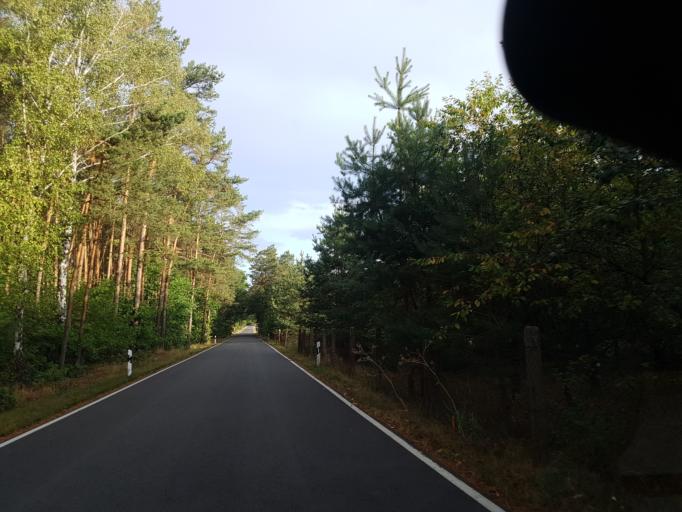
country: DE
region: Saxony-Anhalt
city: Holzdorf
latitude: 51.7884
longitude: 13.1097
